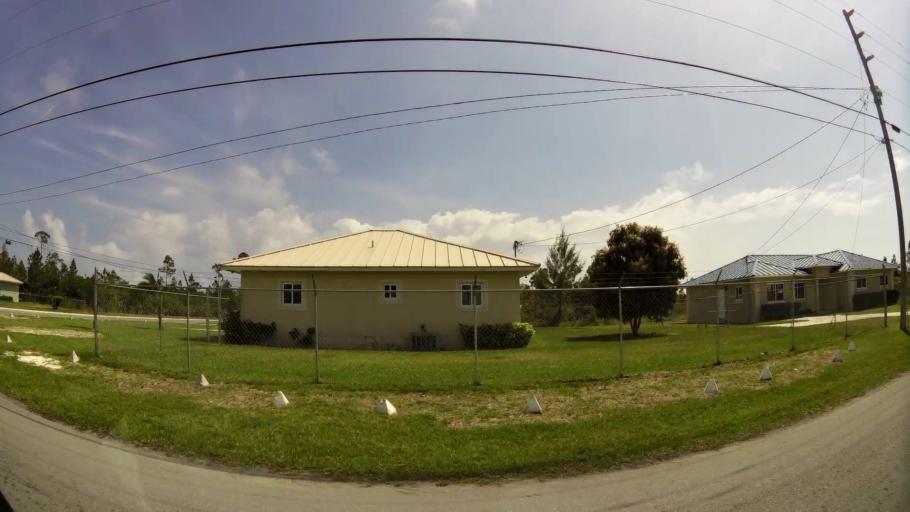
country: BS
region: Freeport
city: Freeport
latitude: 26.5016
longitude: -78.7206
